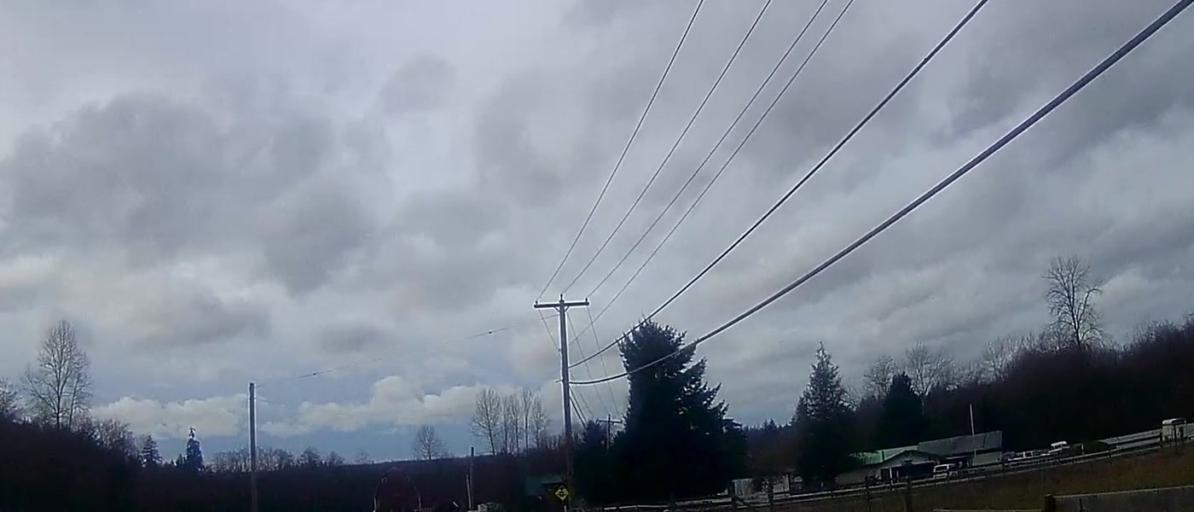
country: US
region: Washington
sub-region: Skagit County
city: Sedro-Woolley
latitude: 48.5833
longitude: -122.2786
